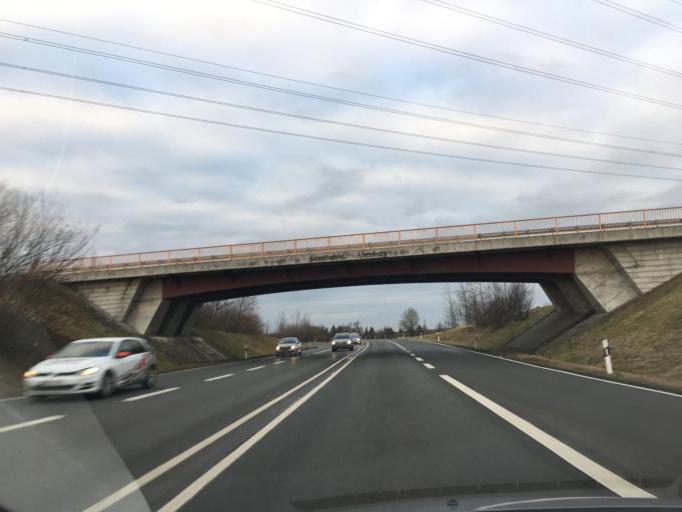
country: DE
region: Thuringia
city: Gerstenberg
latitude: 51.0227
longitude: 12.4559
